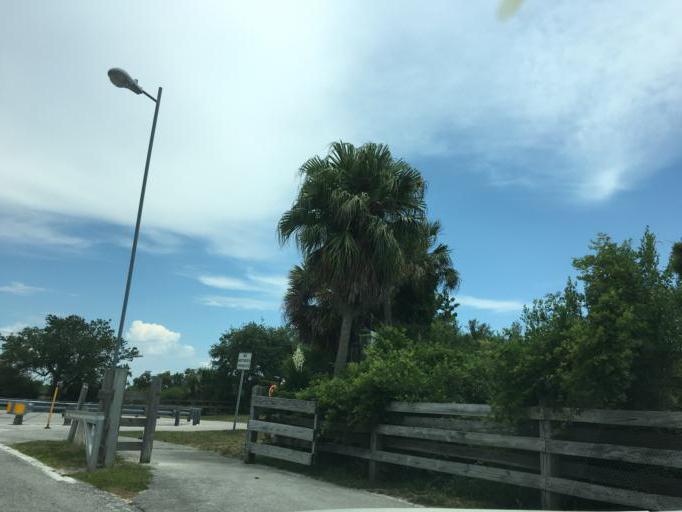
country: US
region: Florida
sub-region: Pinellas County
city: Palm Harbor
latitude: 28.0601
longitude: -82.8177
